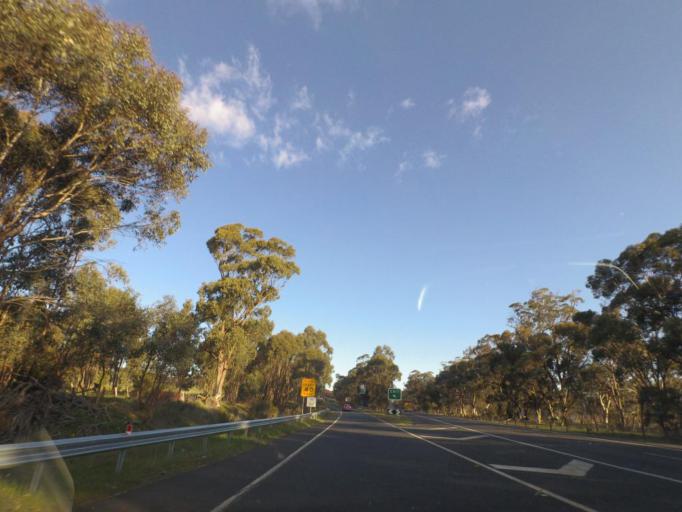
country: AU
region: Victoria
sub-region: Murrindindi
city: Kinglake West
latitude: -37.0607
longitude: 145.1012
